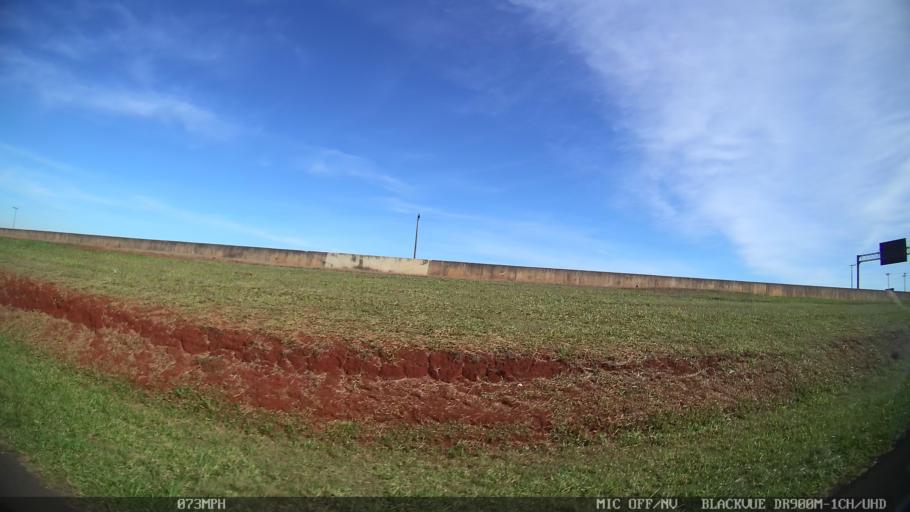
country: BR
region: Sao Paulo
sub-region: Cordeiropolis
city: Cordeiropolis
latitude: -22.4744
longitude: -47.3991
